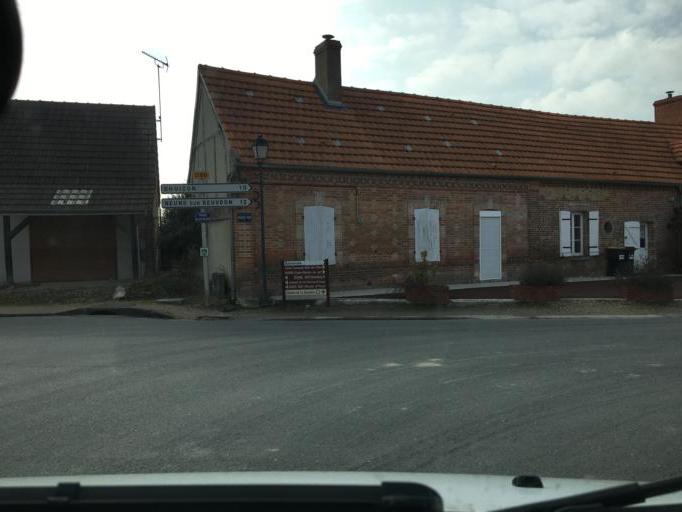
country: FR
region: Centre
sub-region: Departement du Loiret
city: Ligny-le-Ribault
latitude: 47.6229
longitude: 1.7565
